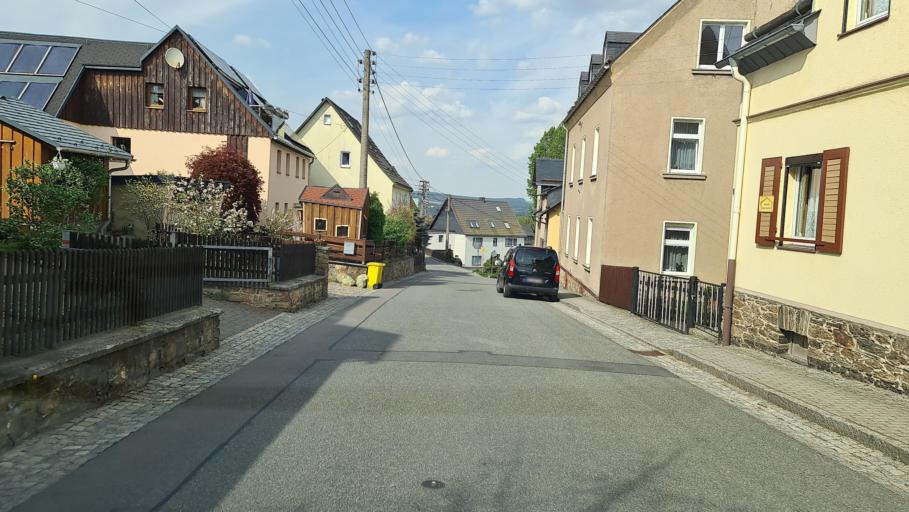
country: DE
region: Saxony
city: Schwarzenberg
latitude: 50.5192
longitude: 12.7736
